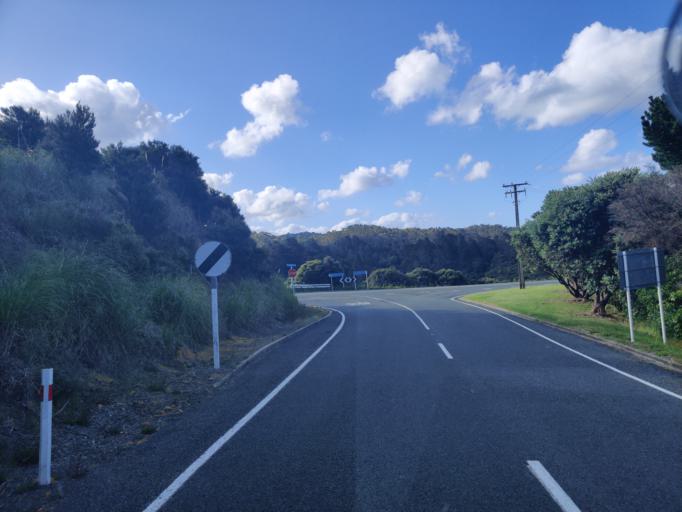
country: NZ
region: Northland
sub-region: Whangarei
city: Ngunguru
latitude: -35.6165
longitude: 174.5206
